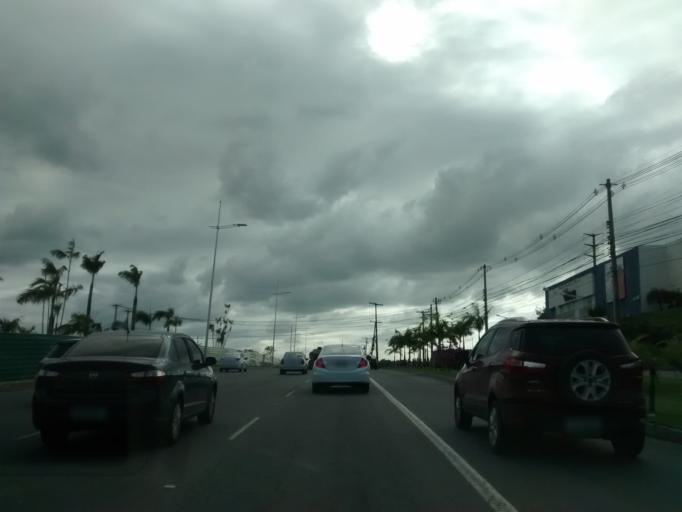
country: BR
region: Bahia
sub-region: Lauro De Freitas
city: Lauro de Freitas
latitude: -12.9294
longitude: -38.3875
